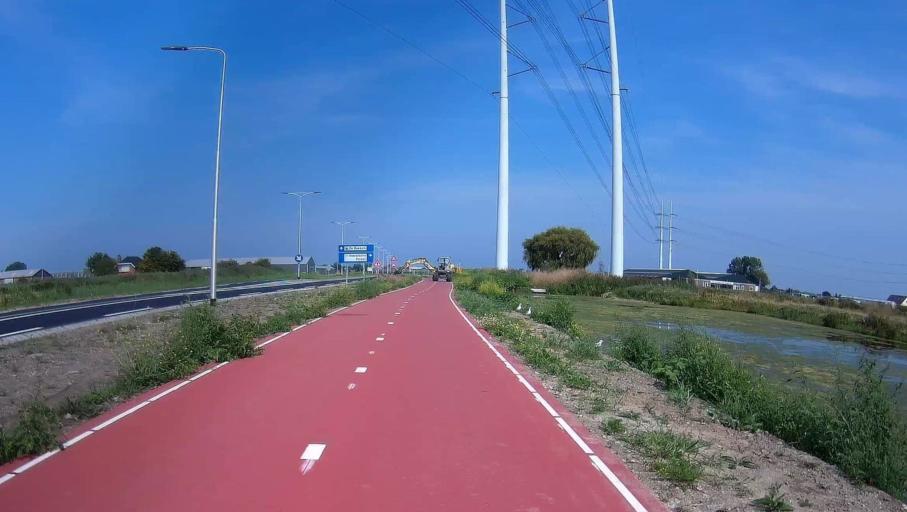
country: NL
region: South Holland
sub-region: Gemeente Pijnacker-Nootdorp
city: Pijnacker
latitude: 52.0155
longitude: 4.4575
